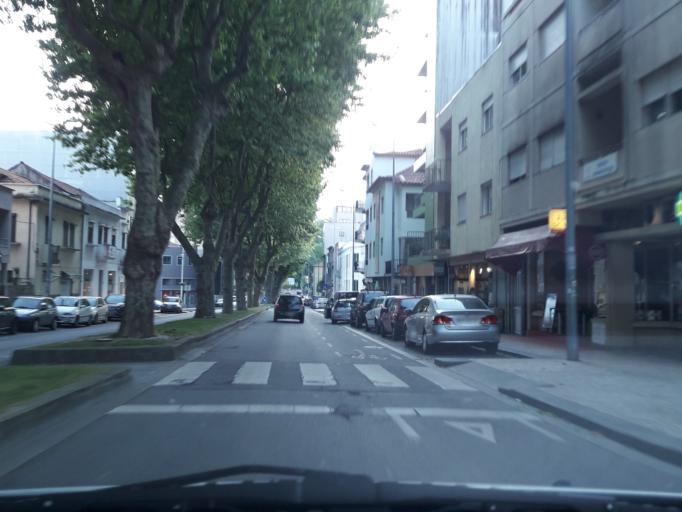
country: PT
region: Braga
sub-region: Vila Nova de Famalicao
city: Vila Nova de Famalicao
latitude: 41.4085
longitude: -8.5200
